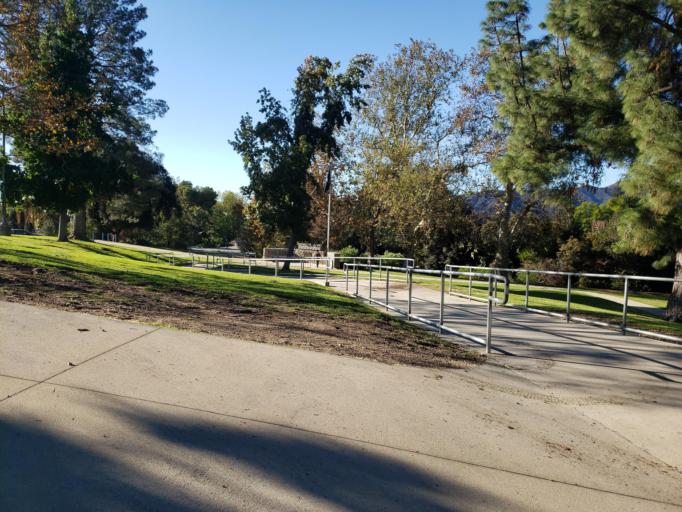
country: US
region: California
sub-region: Los Angeles County
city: La Crescenta-Montrose
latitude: 34.2331
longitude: -118.2355
